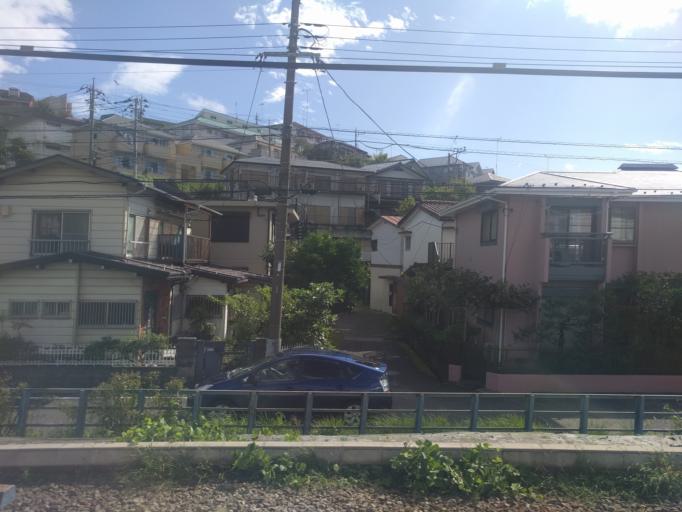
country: JP
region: Tokyo
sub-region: Machida-shi
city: Machida
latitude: 35.5562
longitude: 139.4615
